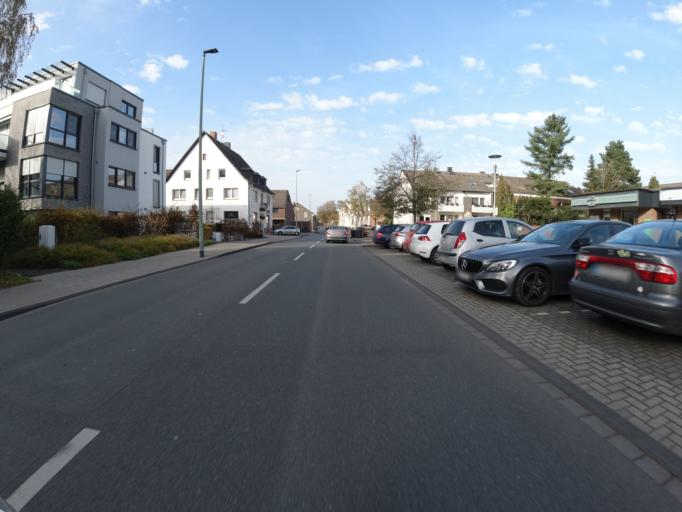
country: DE
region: North Rhine-Westphalia
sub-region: Regierungsbezirk Dusseldorf
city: Moers
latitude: 51.3989
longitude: 6.6682
